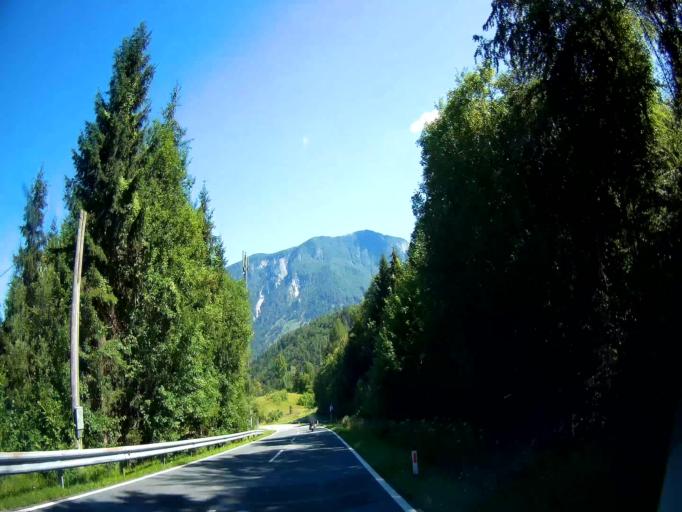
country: AT
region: Carinthia
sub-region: Politischer Bezirk Volkermarkt
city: Gallizien
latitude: 46.5542
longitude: 14.4903
